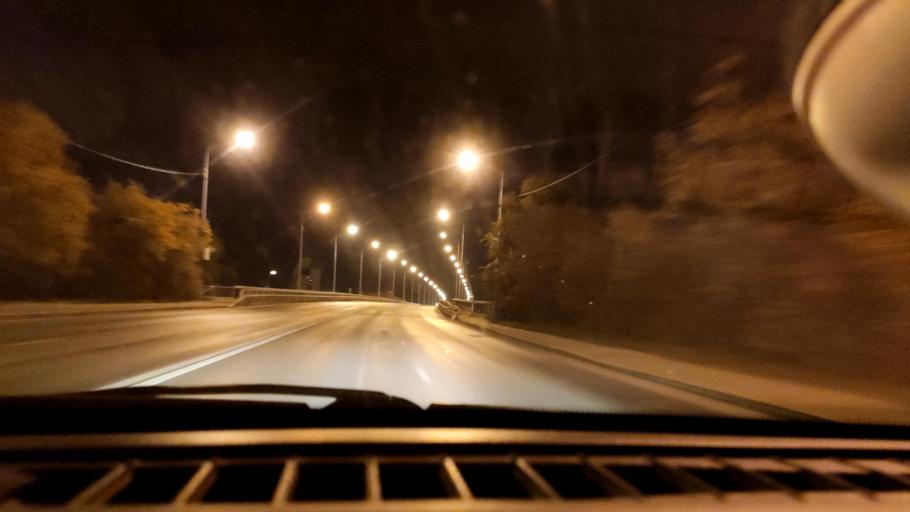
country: RU
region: Samara
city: Samara
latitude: 53.1776
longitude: 50.1930
